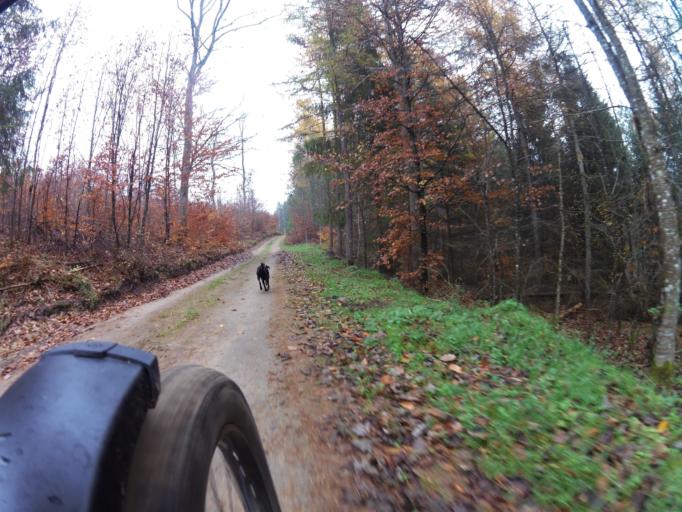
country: PL
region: Pomeranian Voivodeship
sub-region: Powiat wejherowski
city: Orle
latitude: 54.6990
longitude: 18.1550
